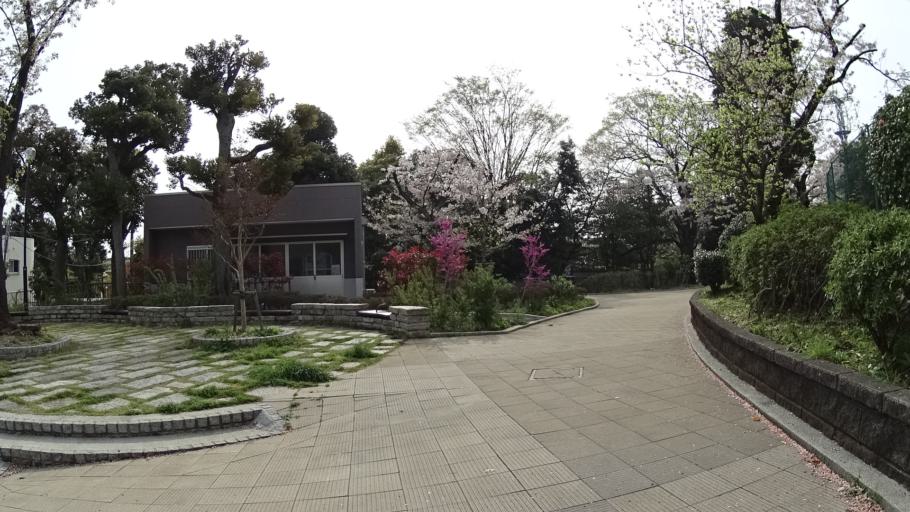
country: JP
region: Kanagawa
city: Yokohama
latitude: 35.4463
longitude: 139.6234
